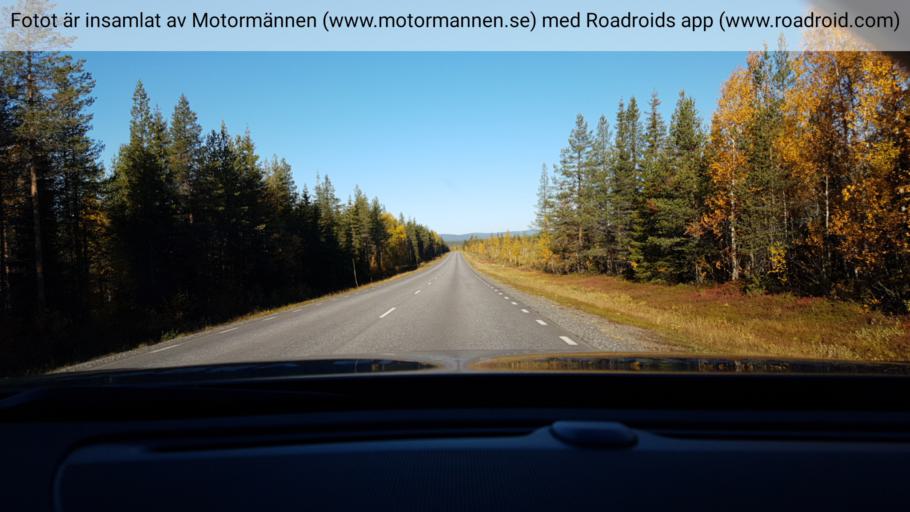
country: SE
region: Vaesterbotten
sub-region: Skelleftea Kommun
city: Storvik
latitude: 65.3648
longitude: 20.4183
